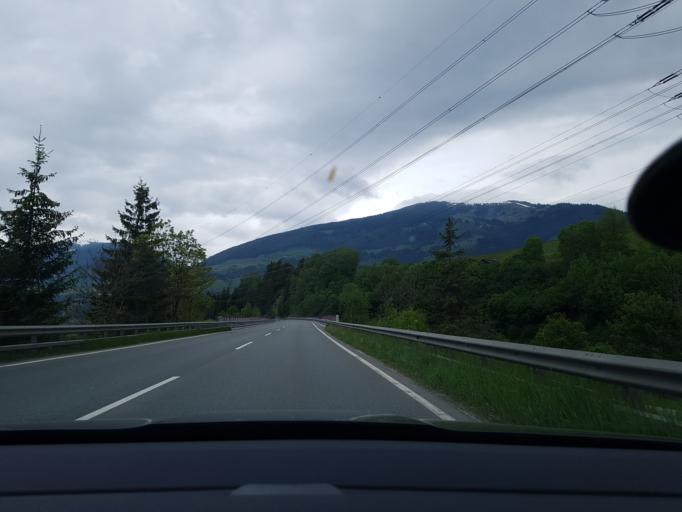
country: AT
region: Salzburg
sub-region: Politischer Bezirk Zell am See
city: Hollersbach im Pinzgau
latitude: 47.2775
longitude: 12.4219
